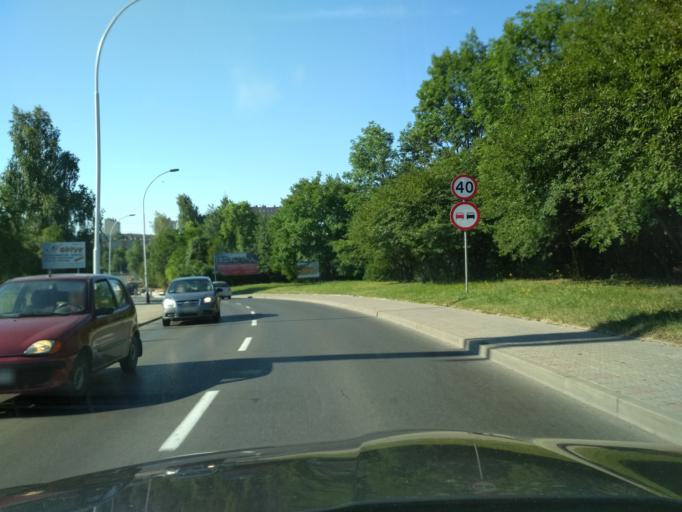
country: PL
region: Subcarpathian Voivodeship
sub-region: Rzeszow
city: Rzeszow
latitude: 50.0581
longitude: 21.9772
